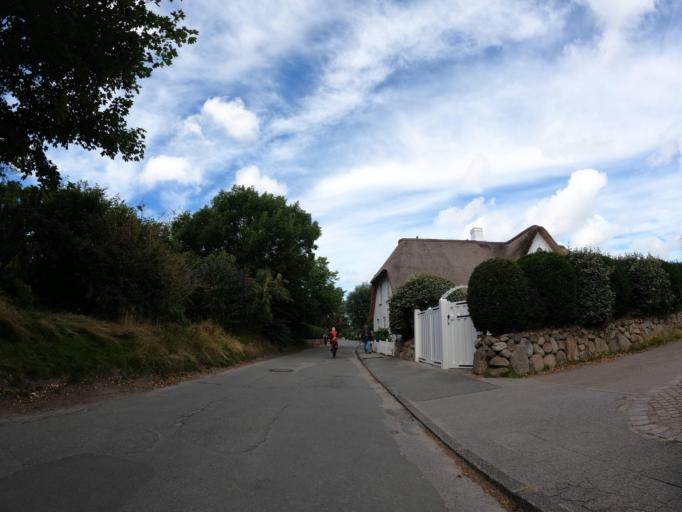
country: DE
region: Schleswig-Holstein
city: Keitum
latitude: 54.8997
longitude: 8.3680
